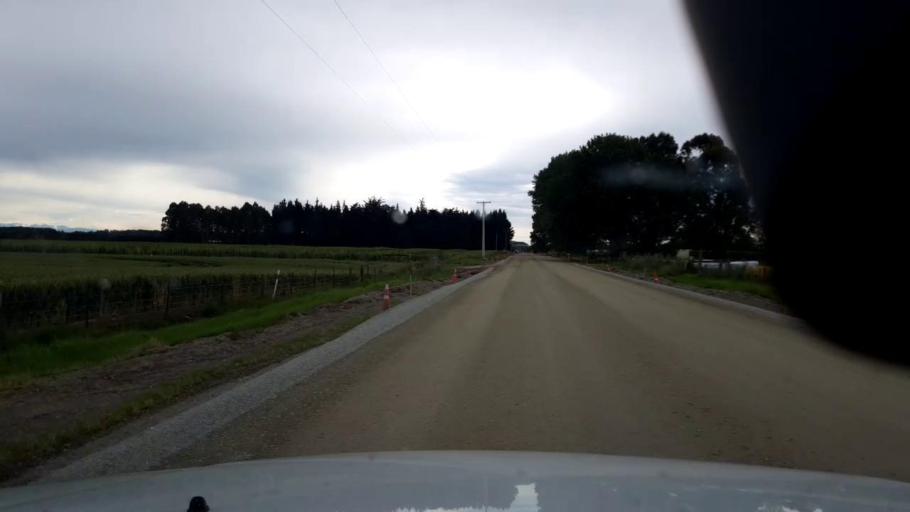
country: NZ
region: Canterbury
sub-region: Timaru District
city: Pleasant Point
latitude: -44.2784
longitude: 171.2483
